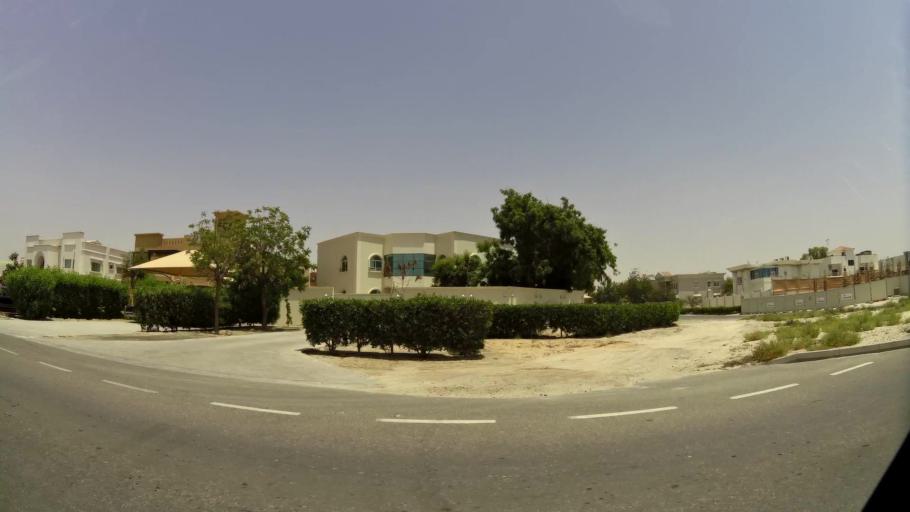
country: AE
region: Dubai
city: Dubai
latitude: 25.1683
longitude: 55.2187
